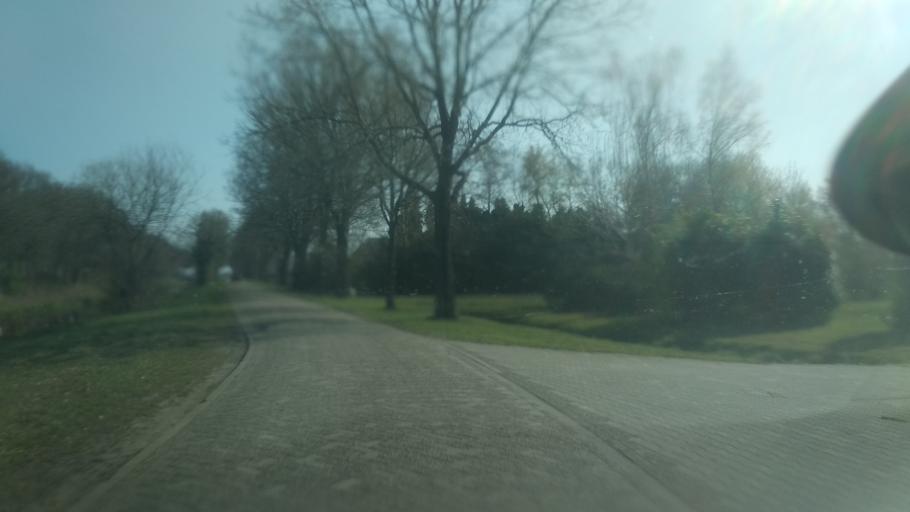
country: NL
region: Drenthe
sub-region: Gemeente Borger-Odoorn
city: Borger
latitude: 52.8720
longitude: 6.7605
